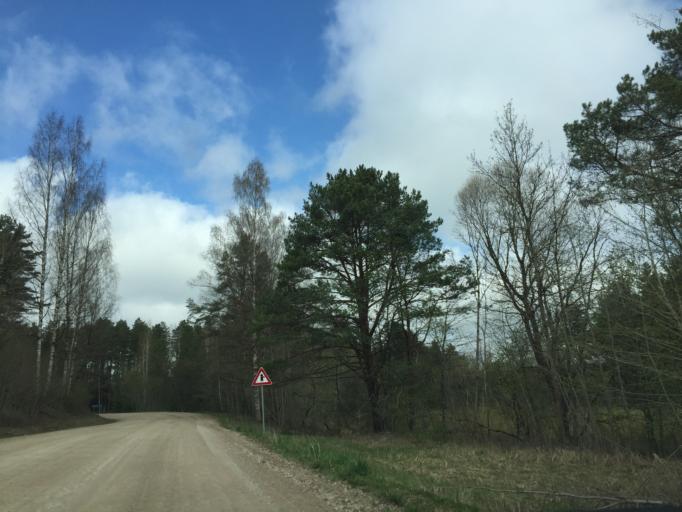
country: LV
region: Apes Novads
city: Ape
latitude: 57.5256
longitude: 26.3782
